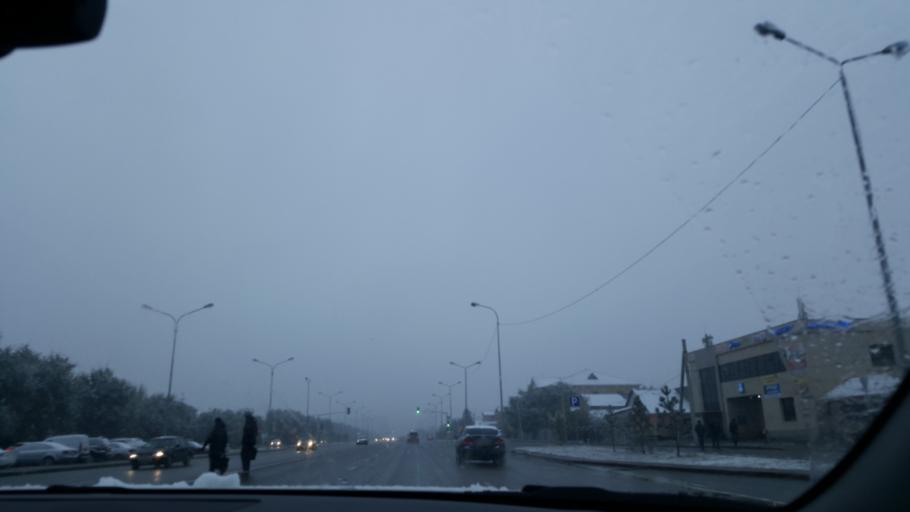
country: KZ
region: Astana Qalasy
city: Astana
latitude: 51.1415
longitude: 71.4882
